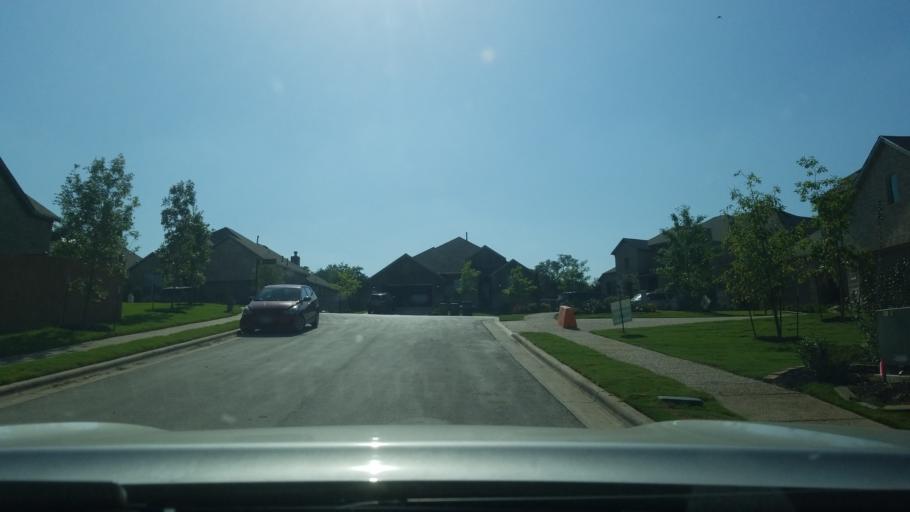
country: US
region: Texas
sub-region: Comal County
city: Bulverde
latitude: 29.7719
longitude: -98.4215
